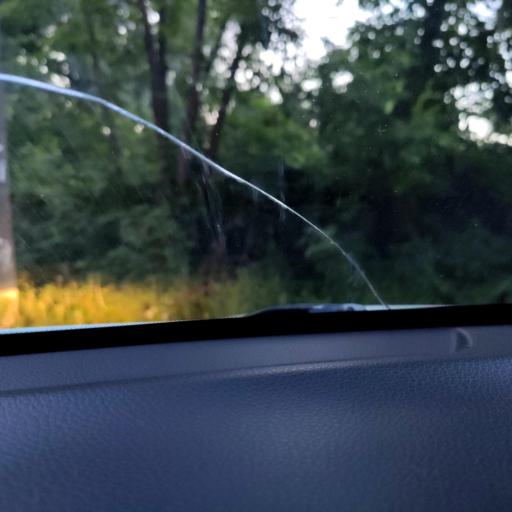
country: RU
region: Tatarstan
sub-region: Gorod Kazan'
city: Kazan
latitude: 55.8481
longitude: 49.1655
